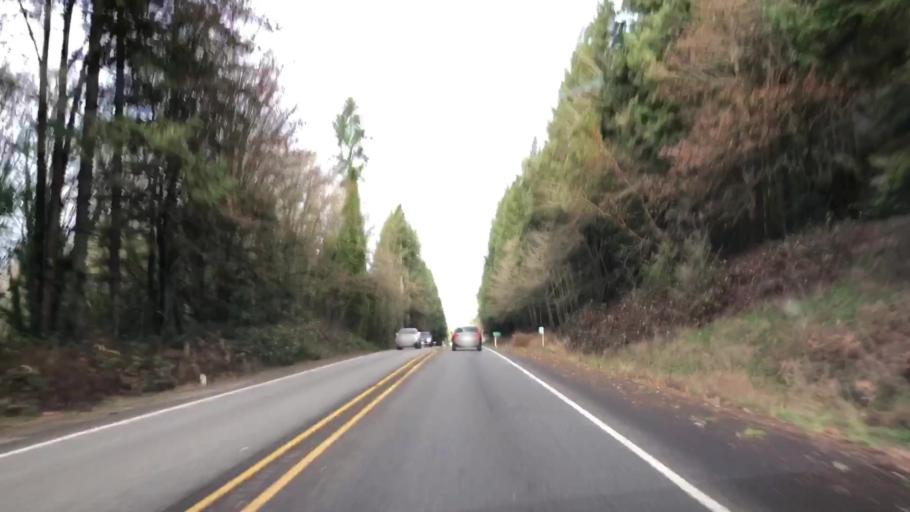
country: US
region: Washington
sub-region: Kitsap County
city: Bainbridge Island
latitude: 47.6755
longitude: -122.5351
